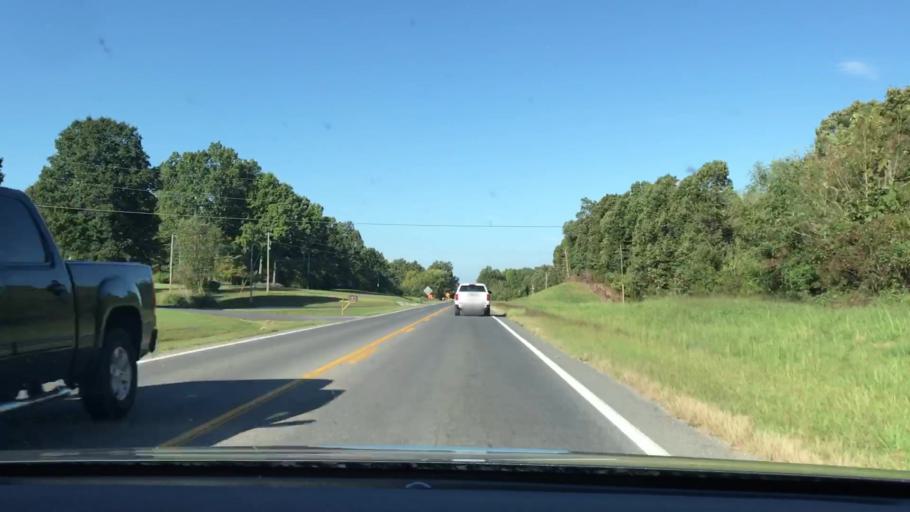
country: US
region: Kentucky
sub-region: Marshall County
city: Calvert City
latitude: 37.0043
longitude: -88.3588
